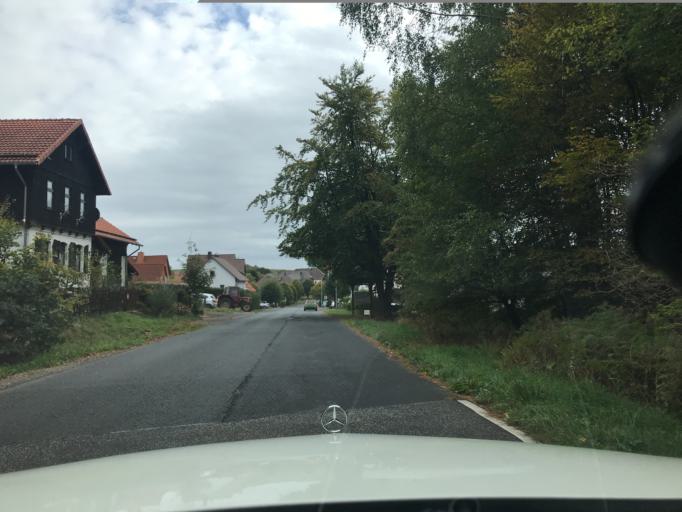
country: DE
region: Hesse
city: Hessisch Lichtenau
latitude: 51.2237
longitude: 9.7414
